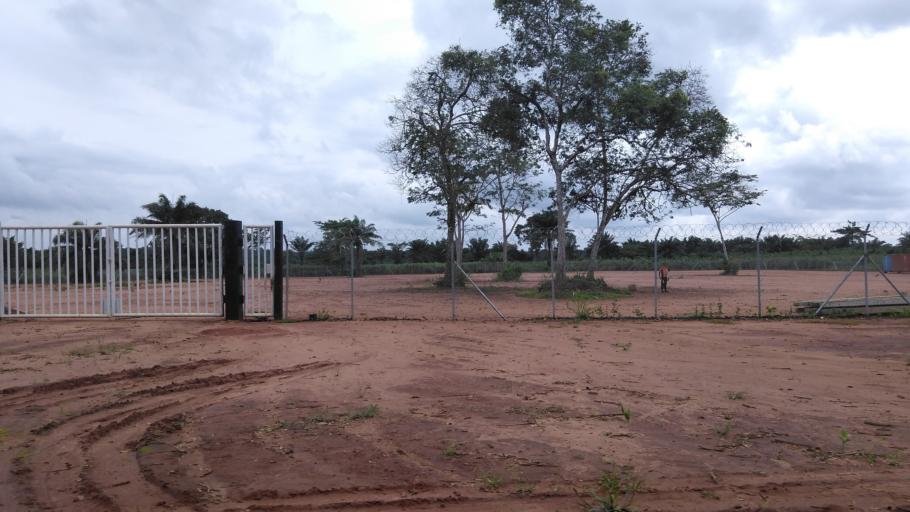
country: NG
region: Ogun
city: Abigi
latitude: 6.5933
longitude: 4.4984
